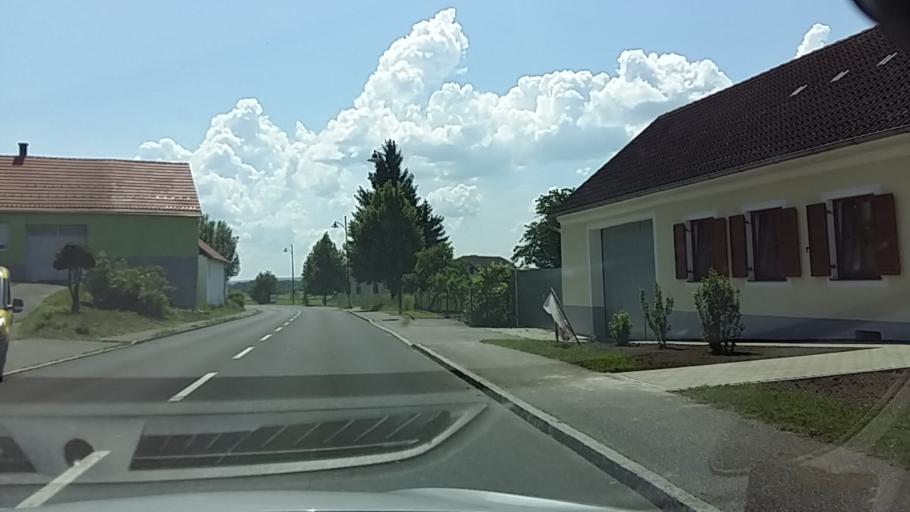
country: AT
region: Burgenland
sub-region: Politischer Bezirk Jennersdorf
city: Heiligenkreuz im Lafnitztal
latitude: 46.9854
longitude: 16.2632
